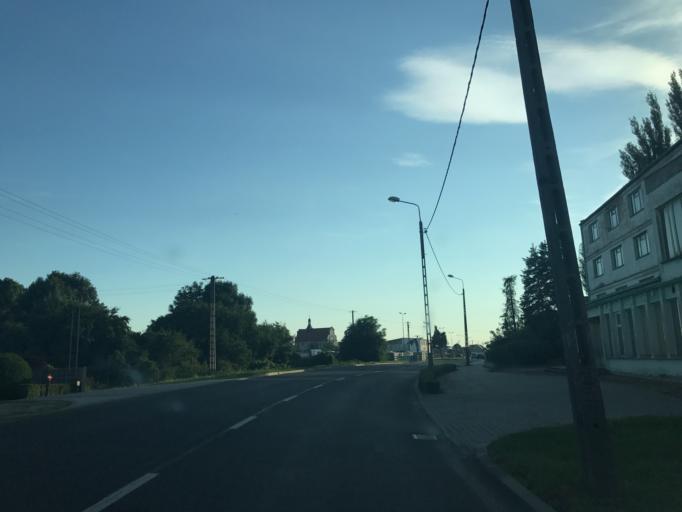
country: PL
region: Greater Poland Voivodeship
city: Miejska Gorka
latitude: 51.6472
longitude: 16.9484
